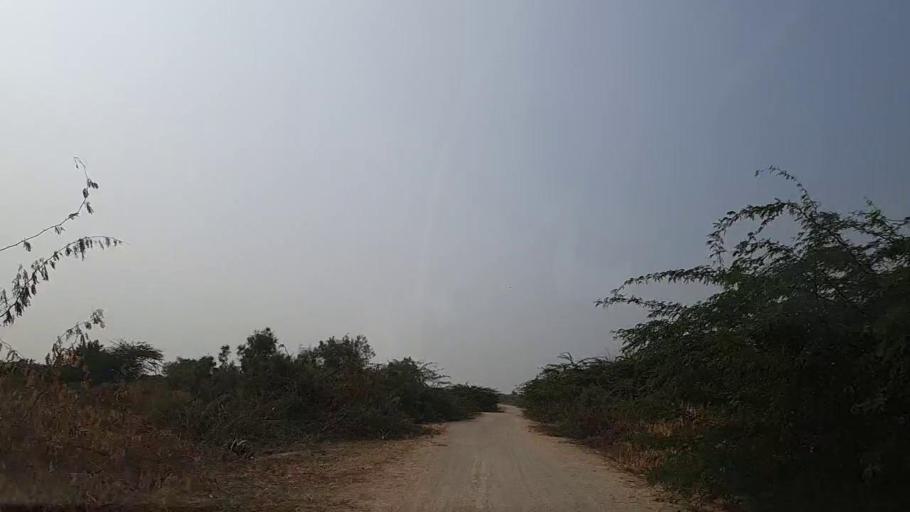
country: PK
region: Sindh
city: Mirpur Sakro
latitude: 24.6040
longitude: 67.7232
